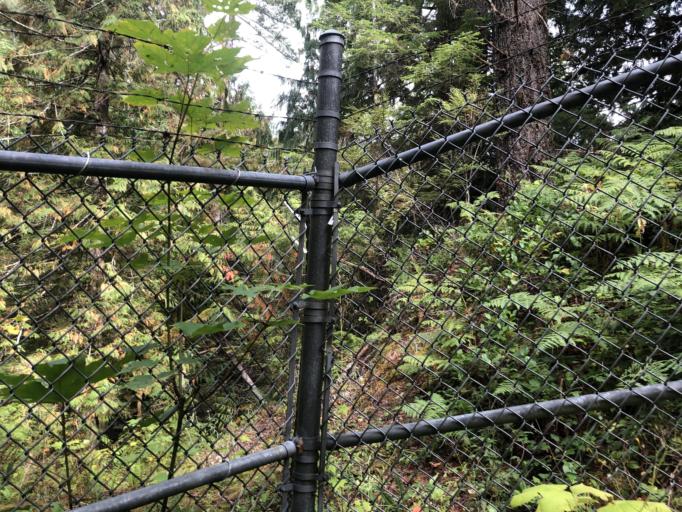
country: CA
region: British Columbia
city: Sooke
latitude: 48.4998
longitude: -123.7102
